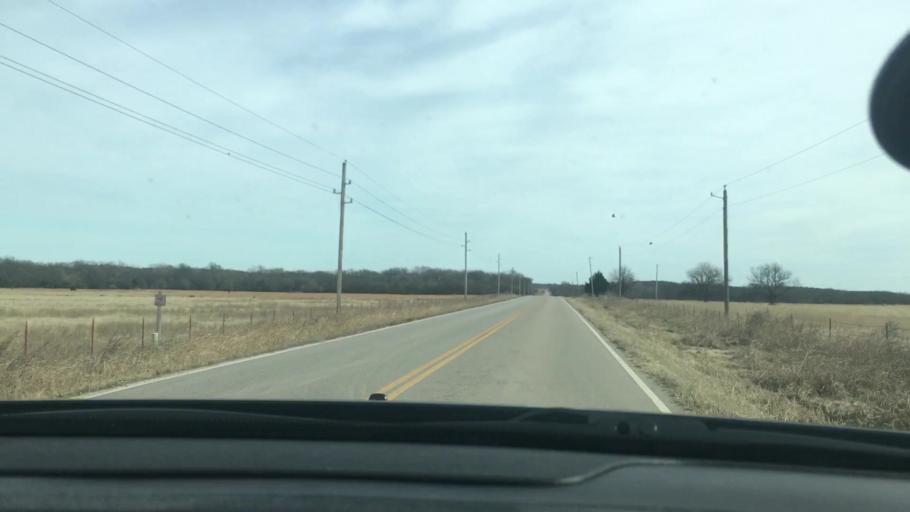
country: US
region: Oklahoma
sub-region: Murray County
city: Sulphur
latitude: 34.4049
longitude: -96.8743
